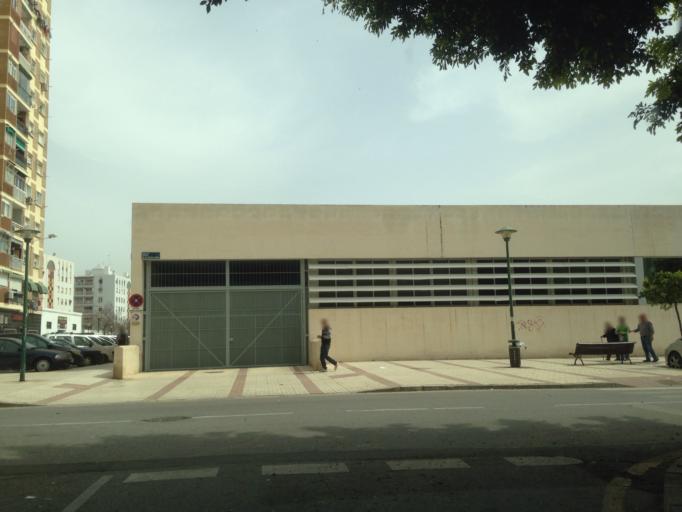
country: ES
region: Andalusia
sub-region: Provincia de Malaga
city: Malaga
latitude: 36.7049
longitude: -4.4348
